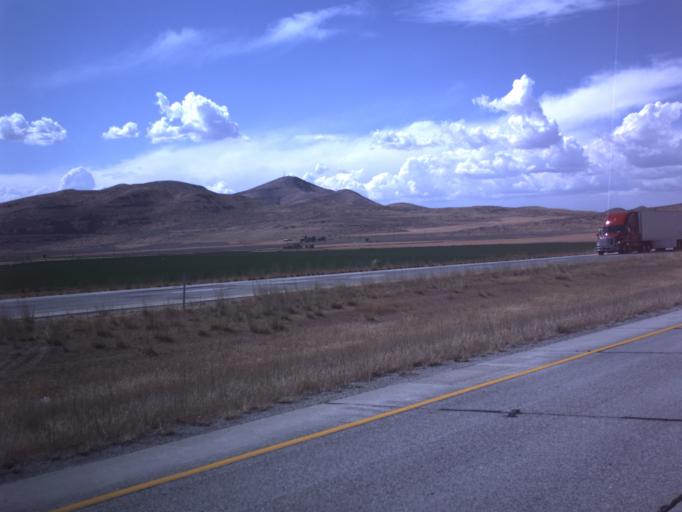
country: US
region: Utah
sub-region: Box Elder County
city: Garland
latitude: 41.7628
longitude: -112.2635
